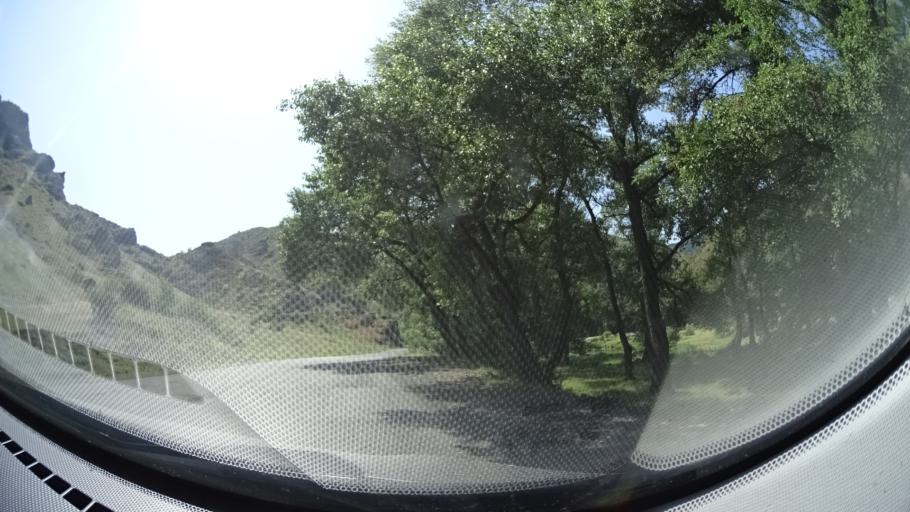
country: GE
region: Samtskhe-Javakheti
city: Akhaltsikhe
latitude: 41.6239
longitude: 43.0671
